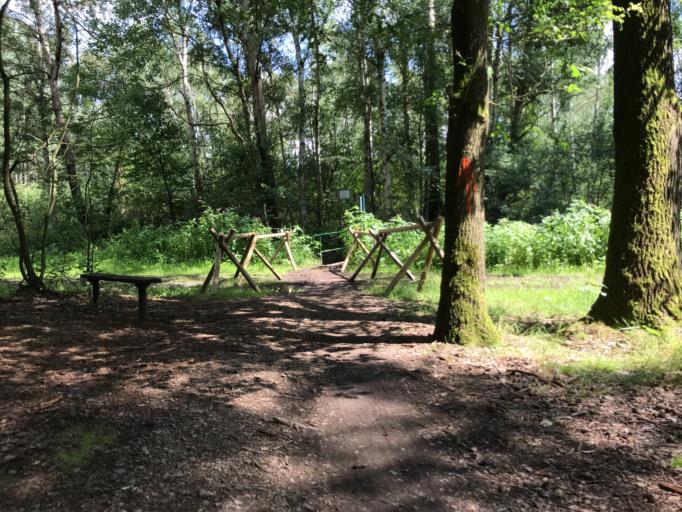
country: CZ
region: Jihocesky
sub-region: Okres Jindrichuv Hradec
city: Trebon
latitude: 48.9936
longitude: 14.7202
